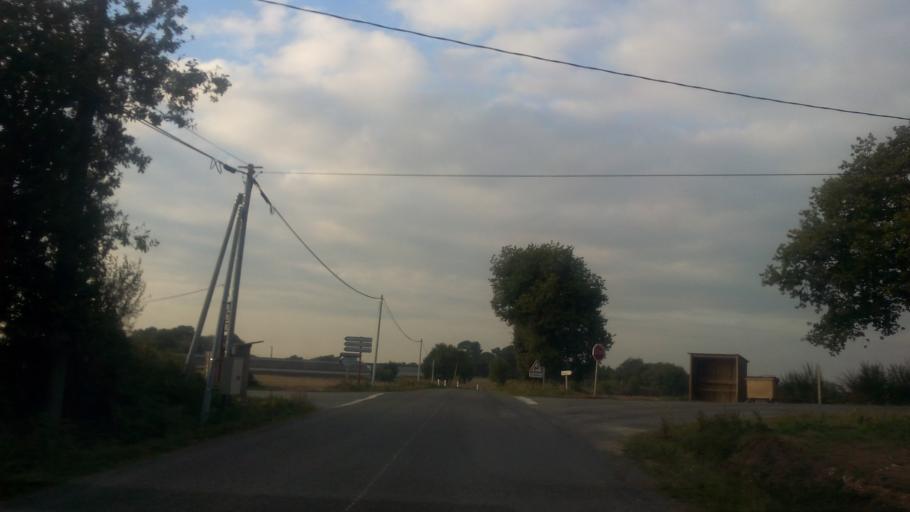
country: FR
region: Brittany
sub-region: Departement du Morbihan
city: Allaire
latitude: 47.6553
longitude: -2.1703
